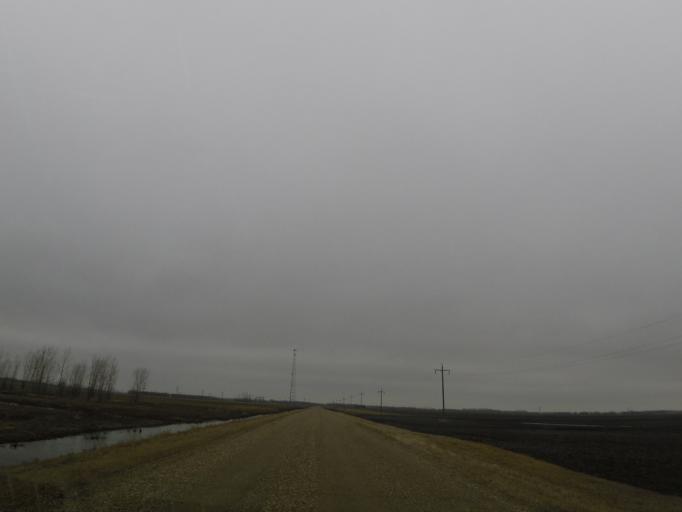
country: US
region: North Dakota
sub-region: Walsh County
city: Grafton
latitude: 48.3532
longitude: -97.1811
